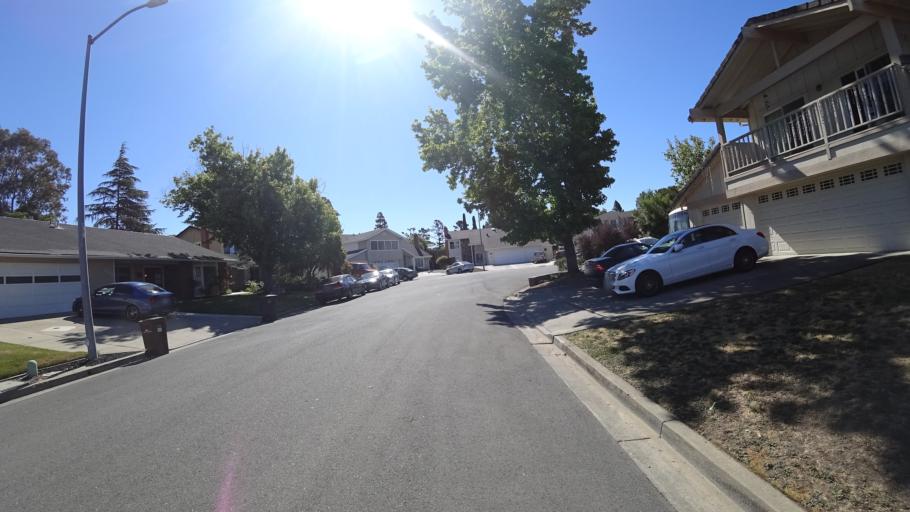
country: US
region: California
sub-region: Alameda County
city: Fairview
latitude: 37.6529
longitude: -122.0280
